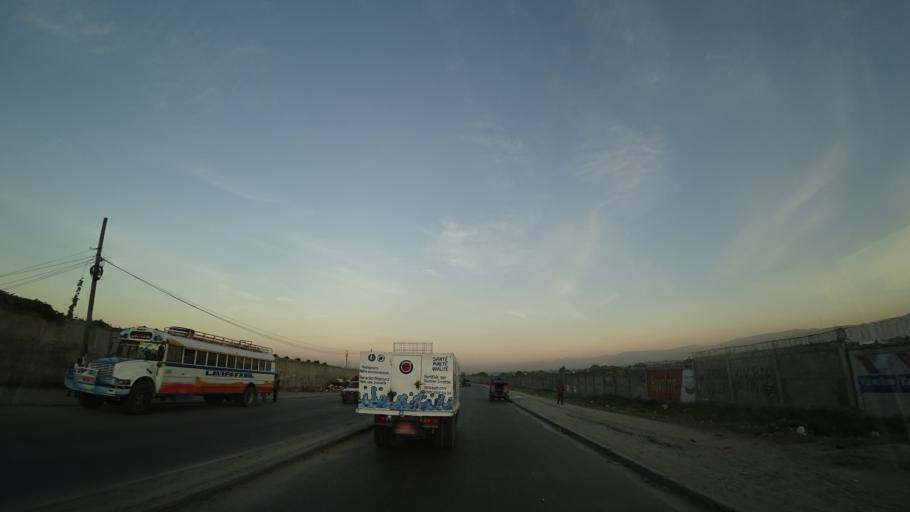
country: HT
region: Ouest
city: Delmas 73
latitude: 18.5770
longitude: -72.3072
